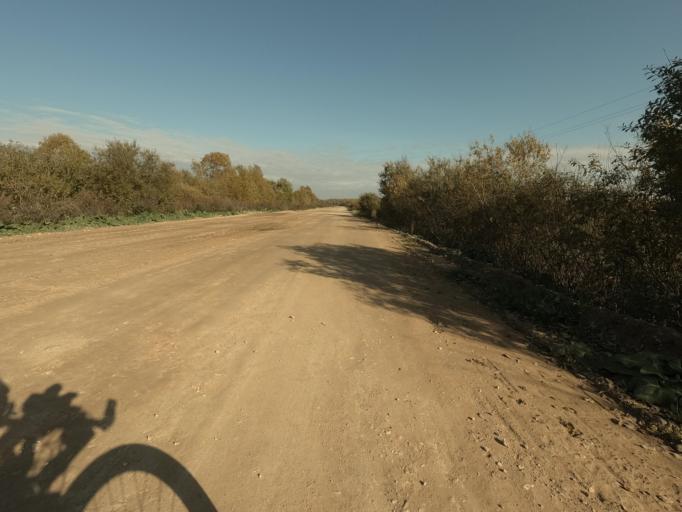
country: RU
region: Novgorod
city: Batetskiy
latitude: 58.8162
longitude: 30.6993
